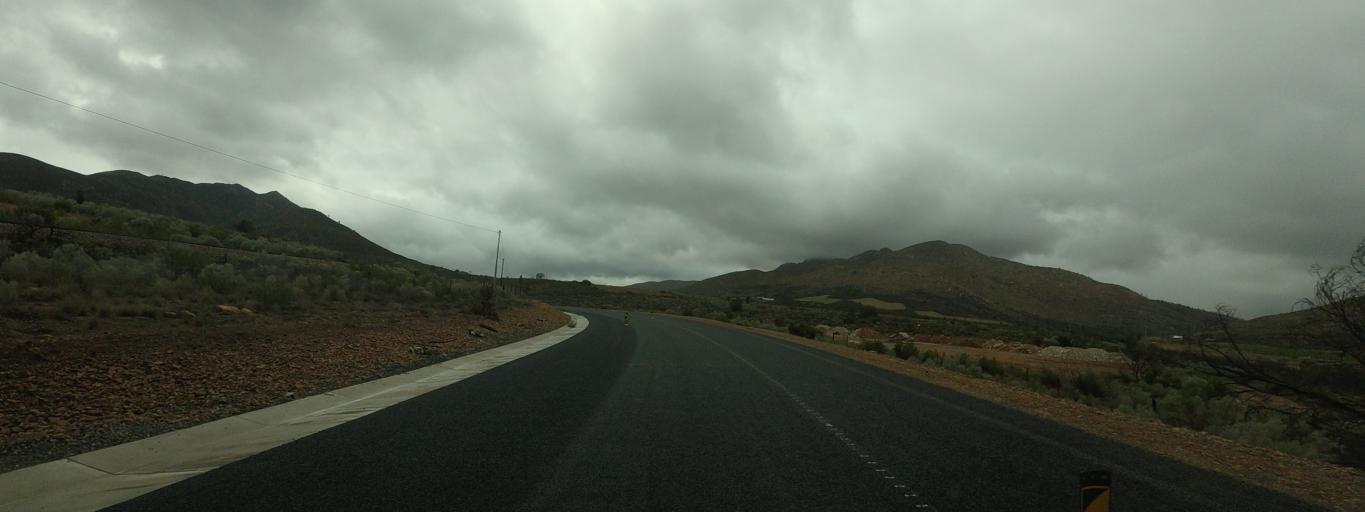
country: ZA
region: Western Cape
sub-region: Eden District Municipality
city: George
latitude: -33.8113
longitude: 22.3420
